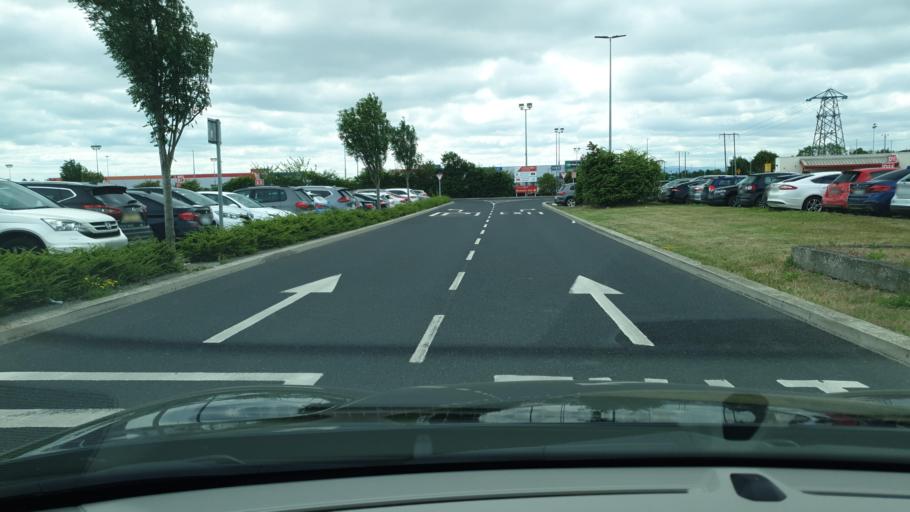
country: IE
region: Leinster
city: Kinsealy-Drinan
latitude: 53.4232
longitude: -6.2258
